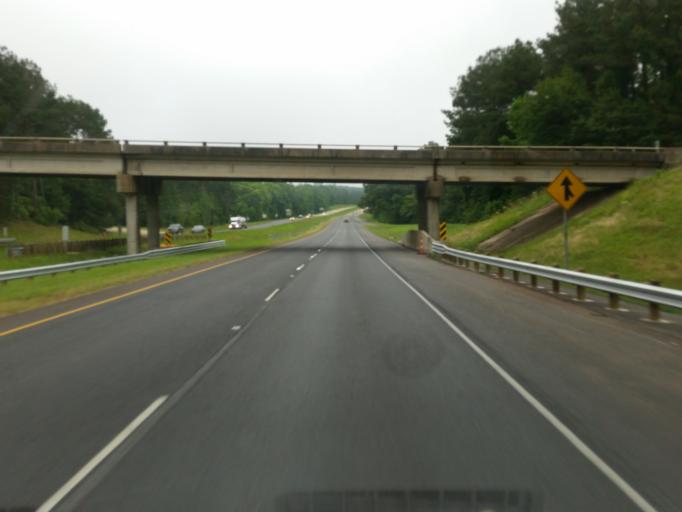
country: US
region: Louisiana
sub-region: Bienville Parish
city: Arcadia
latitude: 32.5632
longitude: -93.0549
